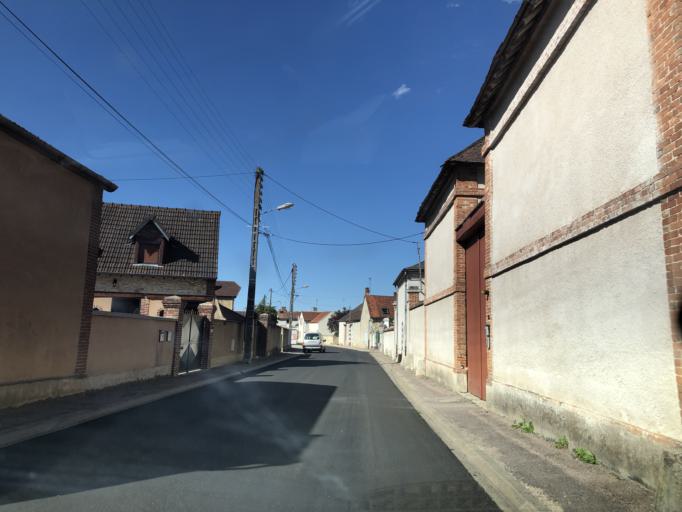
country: FR
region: Bourgogne
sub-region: Departement de l'Yonne
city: Appoigny
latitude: 47.8729
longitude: 3.5265
